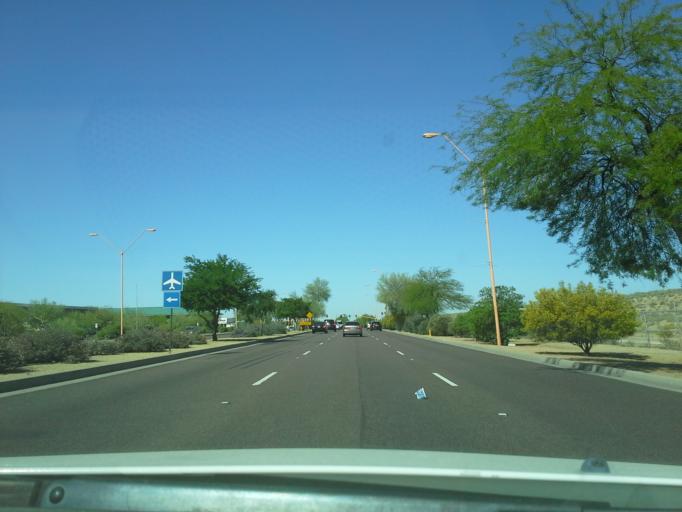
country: US
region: Arizona
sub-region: Maricopa County
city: Paradise Valley
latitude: 33.6339
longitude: -111.9046
